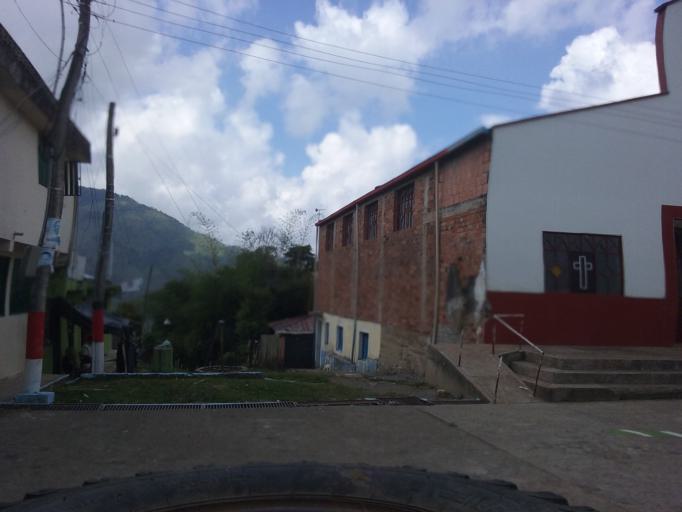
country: CO
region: Tolima
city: Libano
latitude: 4.7977
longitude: -75.0523
